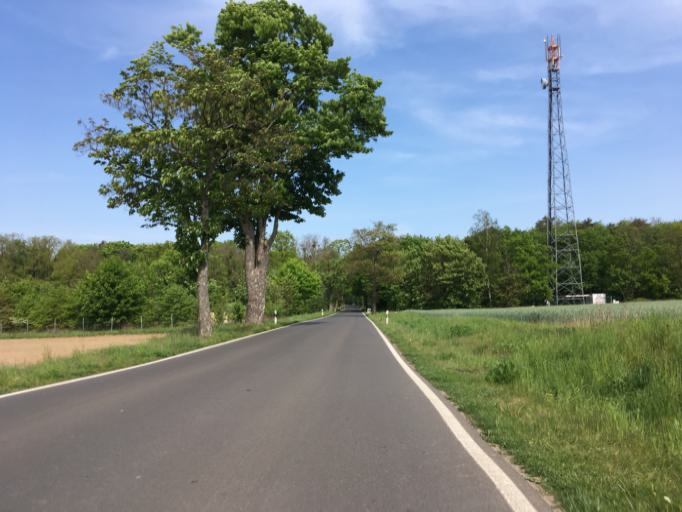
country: DE
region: Brandenburg
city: Werneuchen
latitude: 52.6117
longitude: 13.7561
